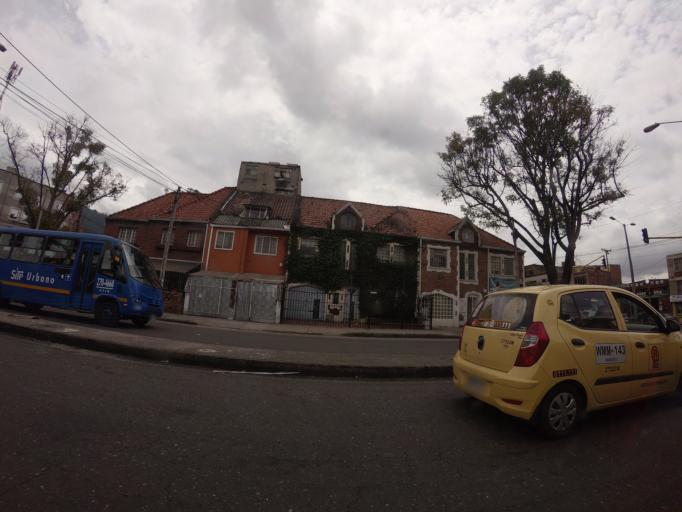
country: CO
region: Bogota D.C.
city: Bogota
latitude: 4.6203
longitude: -74.0746
